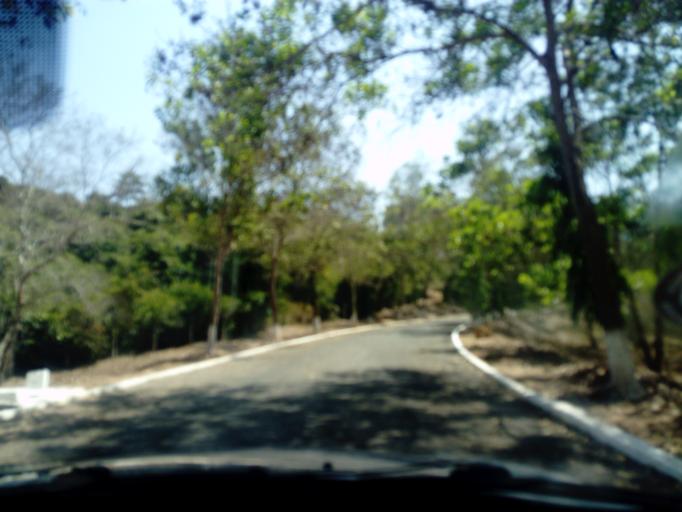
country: GH
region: Central
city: Cape Coast
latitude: 5.1144
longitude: -1.2846
